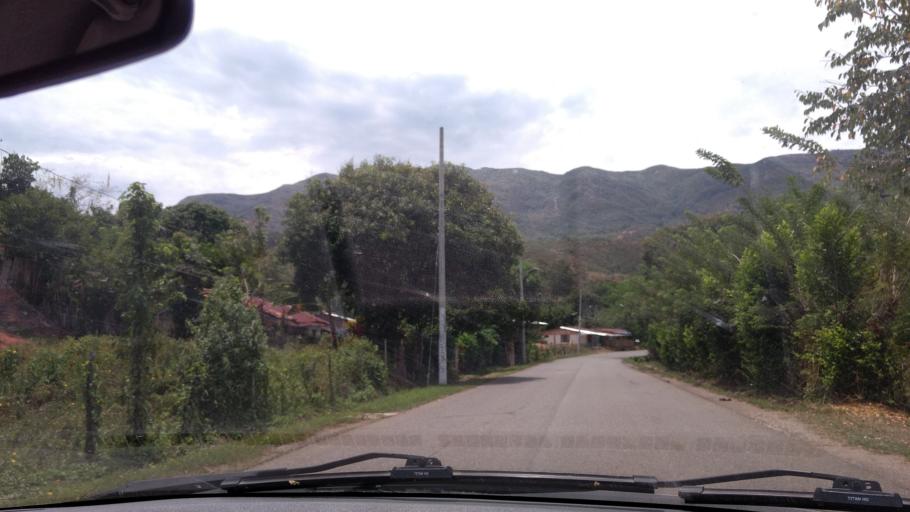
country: CO
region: Cauca
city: Buenos Aires
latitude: 3.0565
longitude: -76.6573
